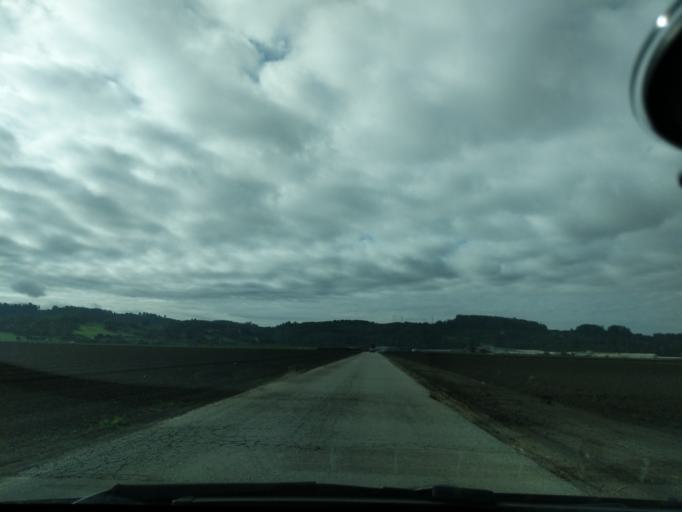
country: US
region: California
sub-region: San Benito County
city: Aromas
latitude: 36.9027
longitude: -121.6705
